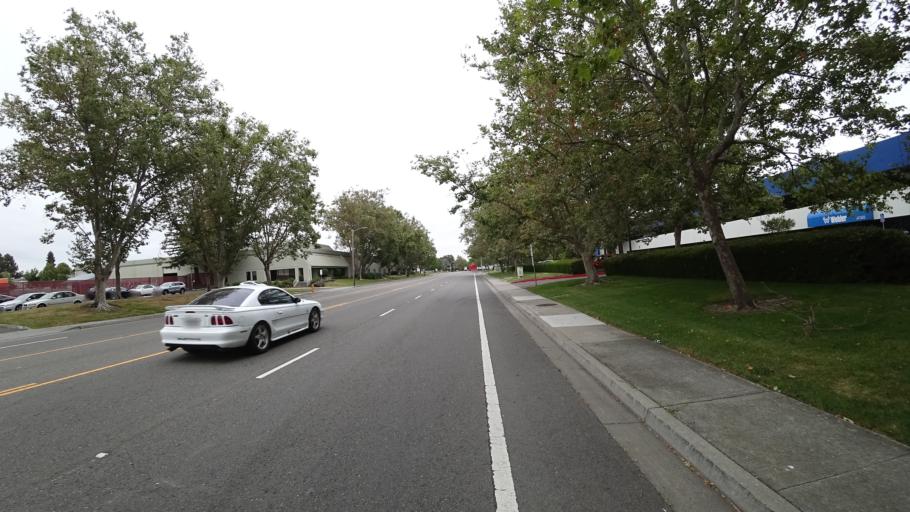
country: US
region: California
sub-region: Alameda County
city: Union City
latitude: 37.6097
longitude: -122.0549
